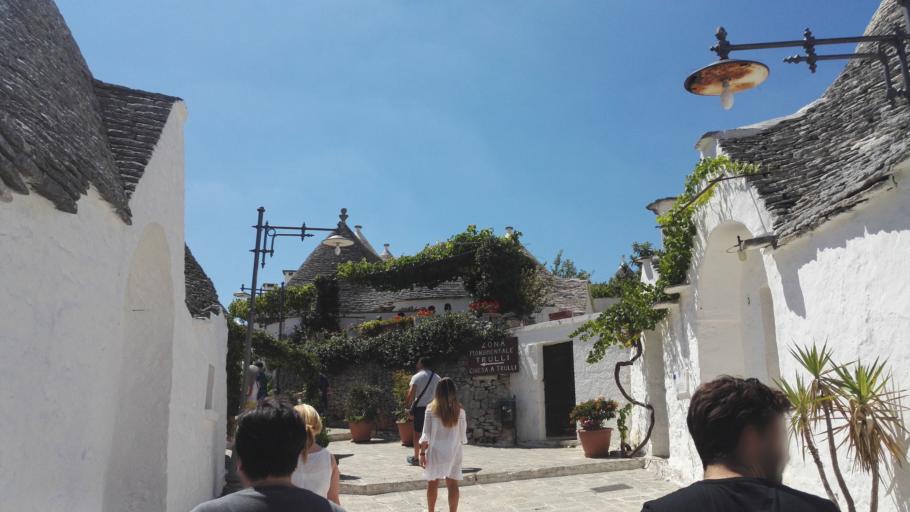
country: IT
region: Apulia
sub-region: Provincia di Bari
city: Alberobello
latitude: 40.7827
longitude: 17.2380
